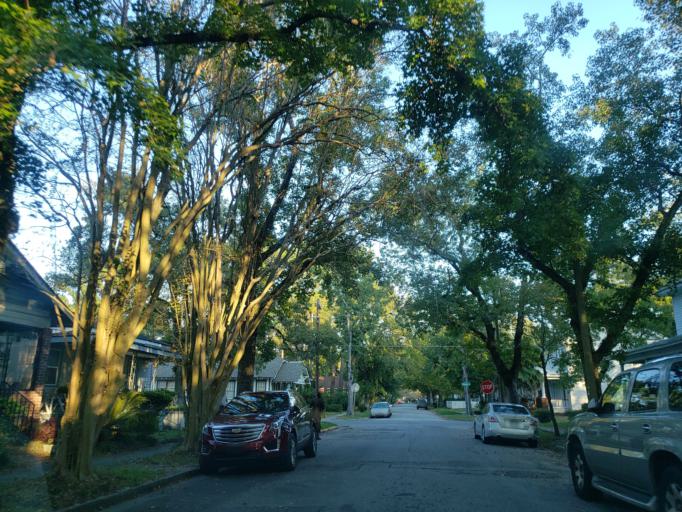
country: US
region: Georgia
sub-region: Chatham County
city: Savannah
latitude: 32.0557
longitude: -81.0875
